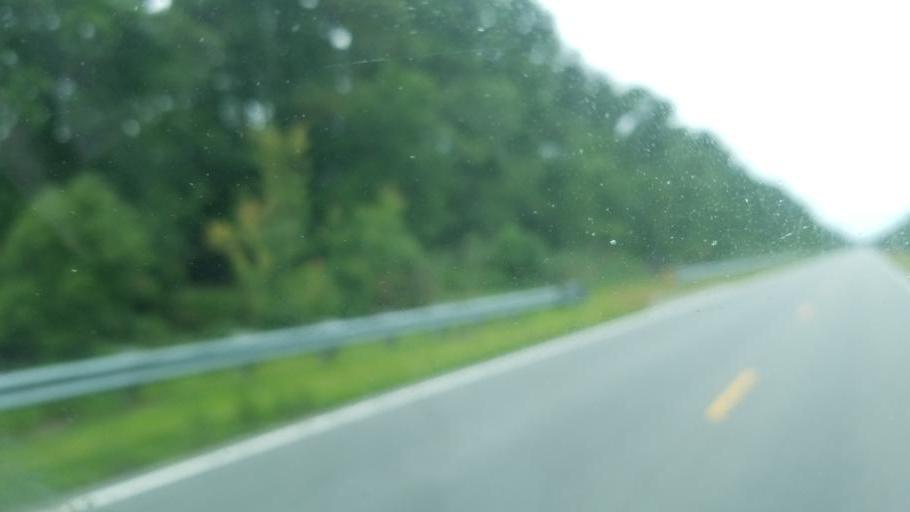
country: US
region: North Carolina
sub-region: Tyrrell County
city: Columbia
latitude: 35.9209
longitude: -76.1294
